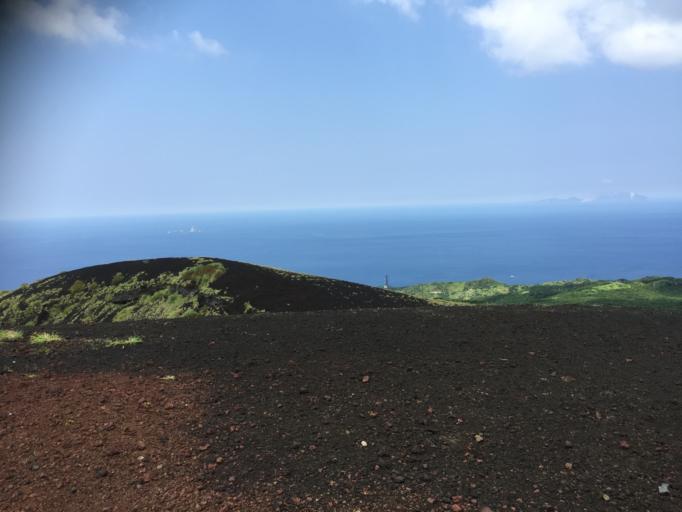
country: JP
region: Shizuoka
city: Shimoda
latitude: 34.0693
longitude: 139.5087
